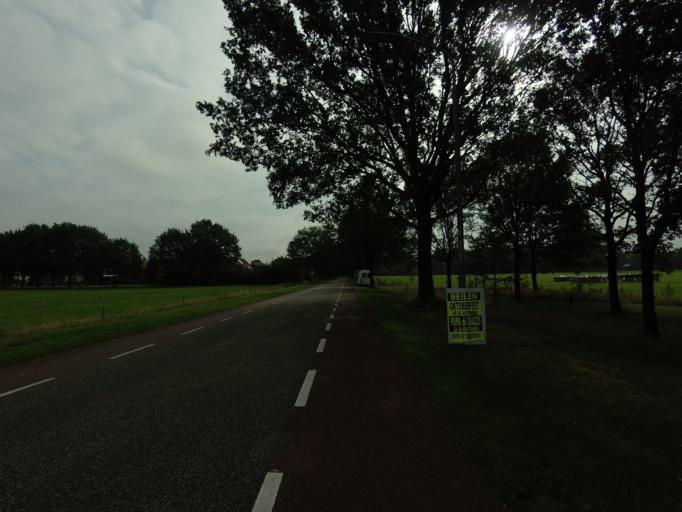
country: NL
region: Drenthe
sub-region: Gemeente Assen
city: Assen
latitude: 52.9193
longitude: 6.5343
